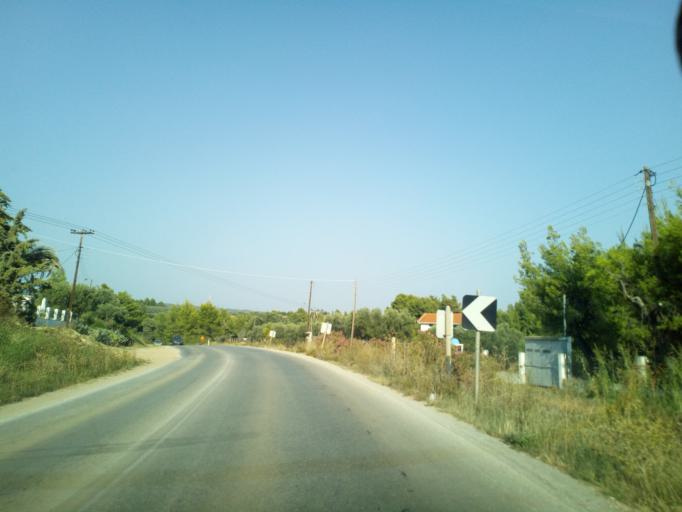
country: GR
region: Central Macedonia
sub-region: Nomos Chalkidikis
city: Nikiti
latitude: 40.2309
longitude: 23.6200
